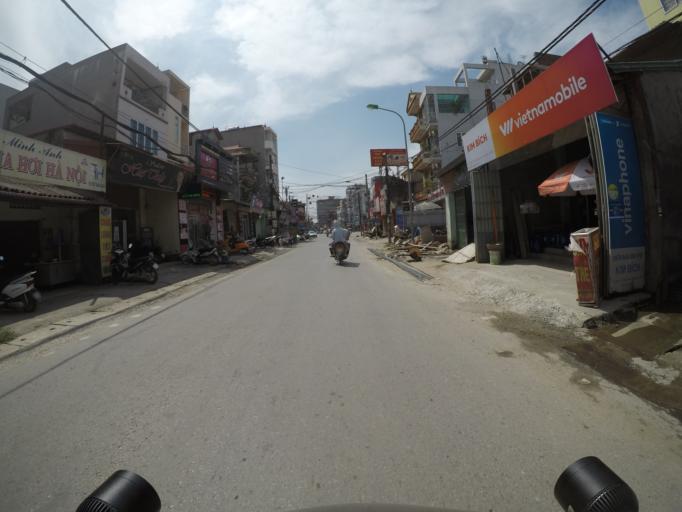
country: VN
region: Ha Noi
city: Troi
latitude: 21.0708
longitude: 105.7081
